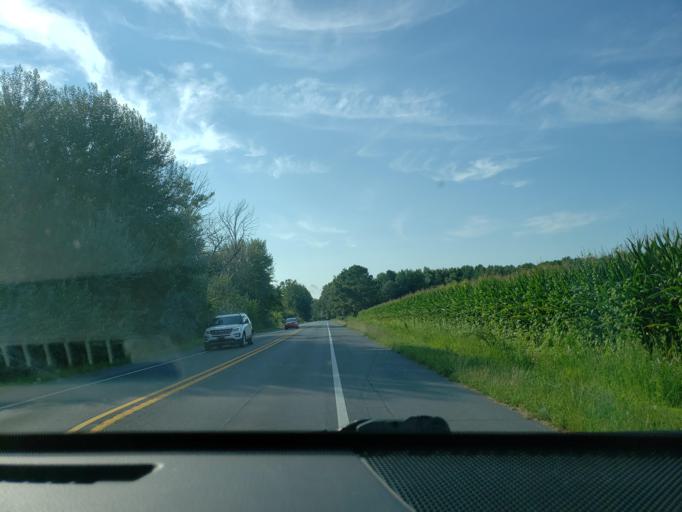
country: US
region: Delaware
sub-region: Sussex County
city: Milton
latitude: 38.7581
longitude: -75.2607
